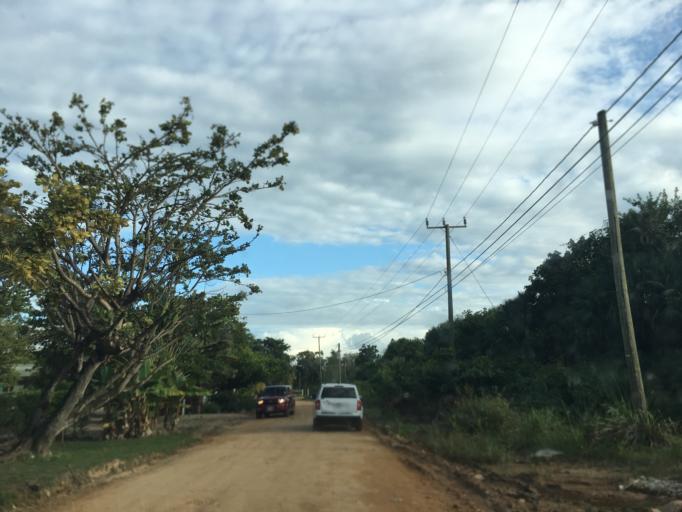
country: BZ
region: Stann Creek
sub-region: Dangriga
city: Dangriga
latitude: 16.8360
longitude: -88.2674
